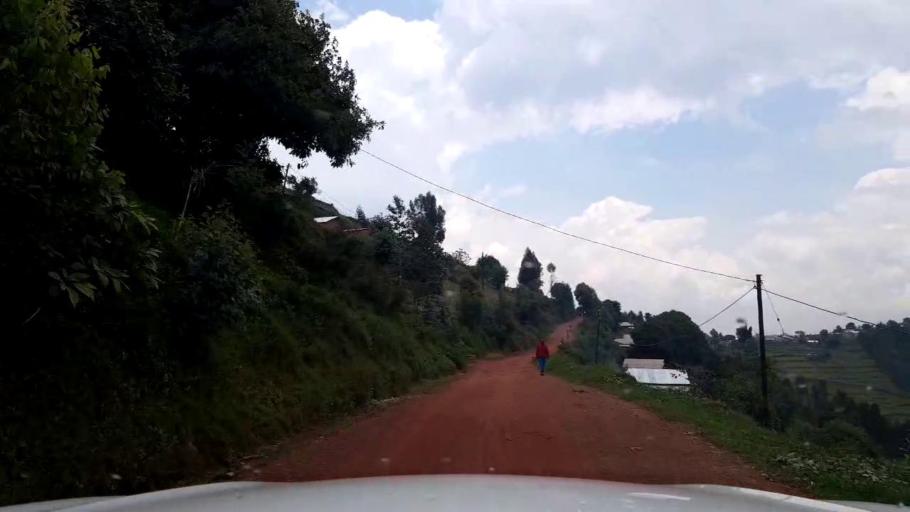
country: RW
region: Northern Province
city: Byumba
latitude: -1.5264
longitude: 29.9572
